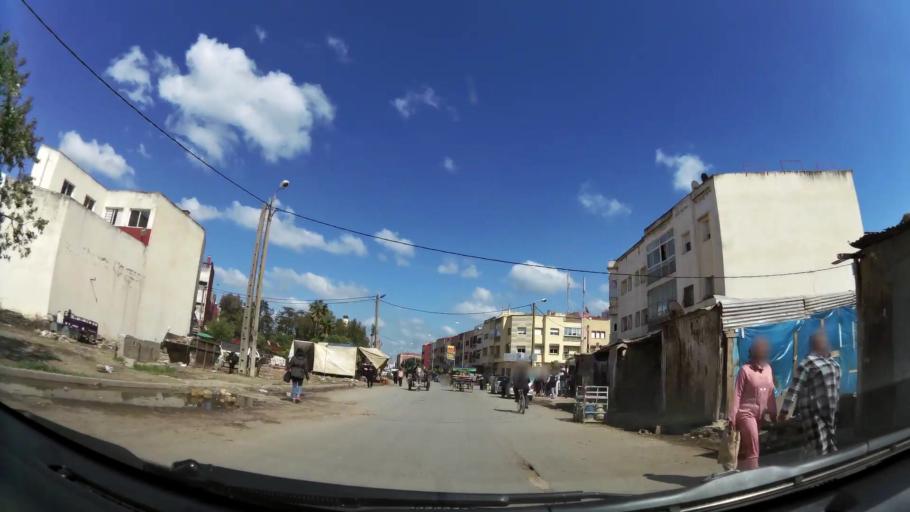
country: MA
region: Grand Casablanca
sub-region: Mediouna
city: Mediouna
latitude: 33.4533
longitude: -7.5132
